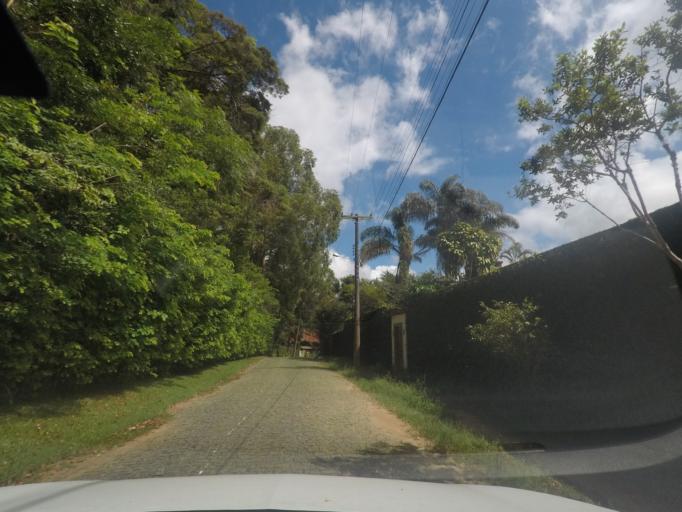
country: BR
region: Rio de Janeiro
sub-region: Teresopolis
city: Teresopolis
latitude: -22.3948
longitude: -42.9879
